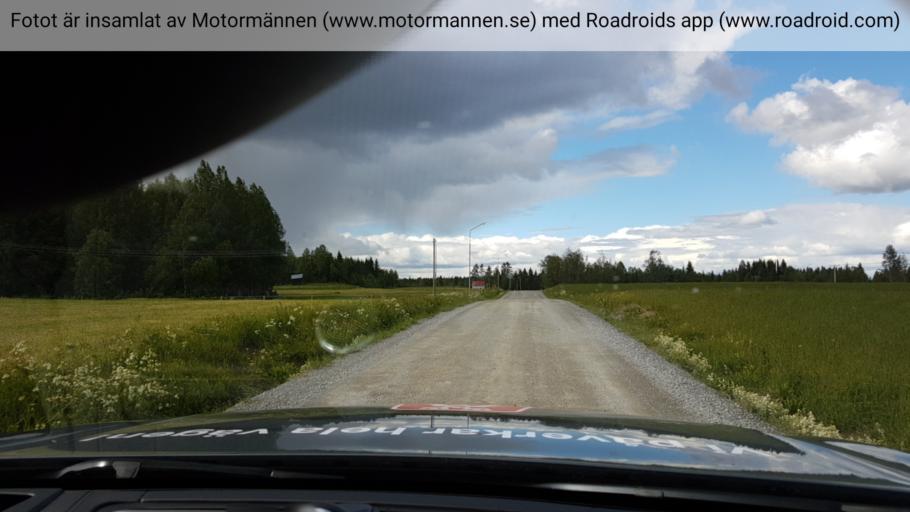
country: SE
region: Jaemtland
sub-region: Bergs Kommun
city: Hoverberg
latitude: 62.9524
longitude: 14.2658
